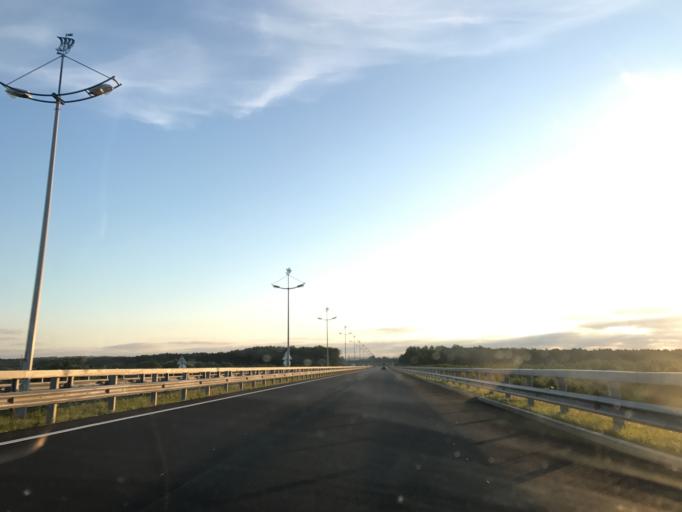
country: RU
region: Kaliningrad
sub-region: Gorod Kaliningrad
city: Pionerskiy
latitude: 54.9200
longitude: 20.2631
